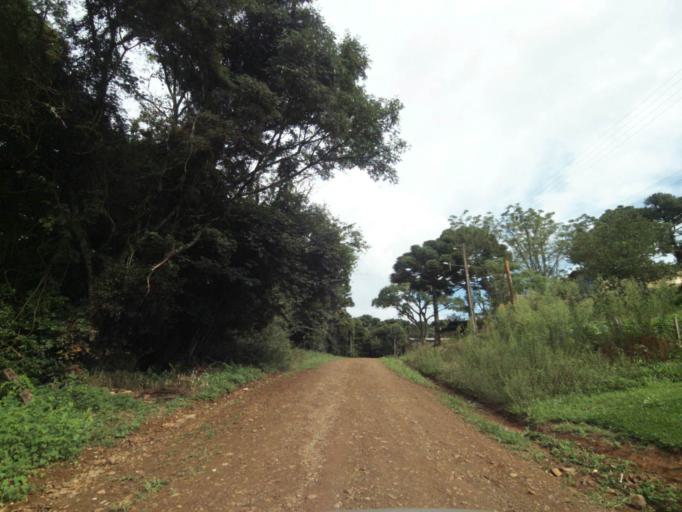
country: BR
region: Rio Grande do Sul
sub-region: Lagoa Vermelha
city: Lagoa Vermelha
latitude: -28.2317
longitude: -51.5091
